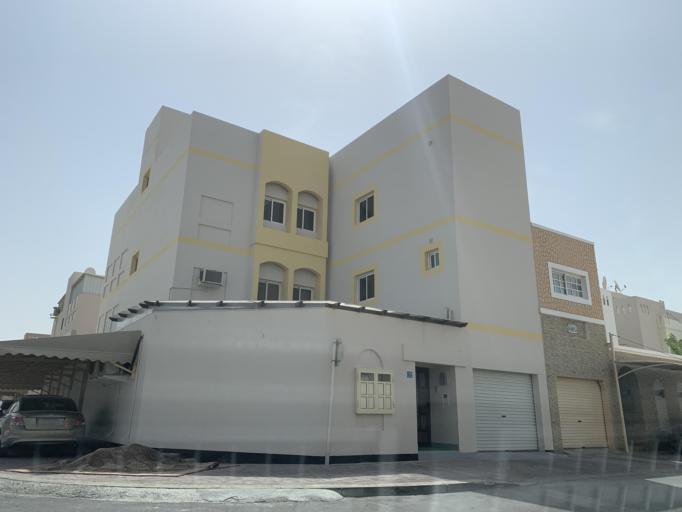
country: BH
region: Northern
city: Madinat `Isa
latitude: 26.1729
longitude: 50.5248
